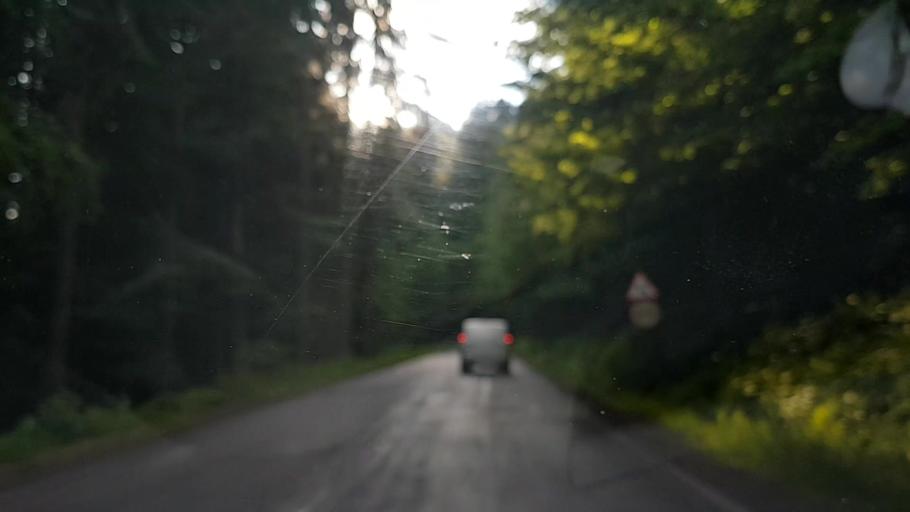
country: RO
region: Harghita
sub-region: Comuna Varsag
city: Varsag
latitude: 46.6655
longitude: 25.3122
